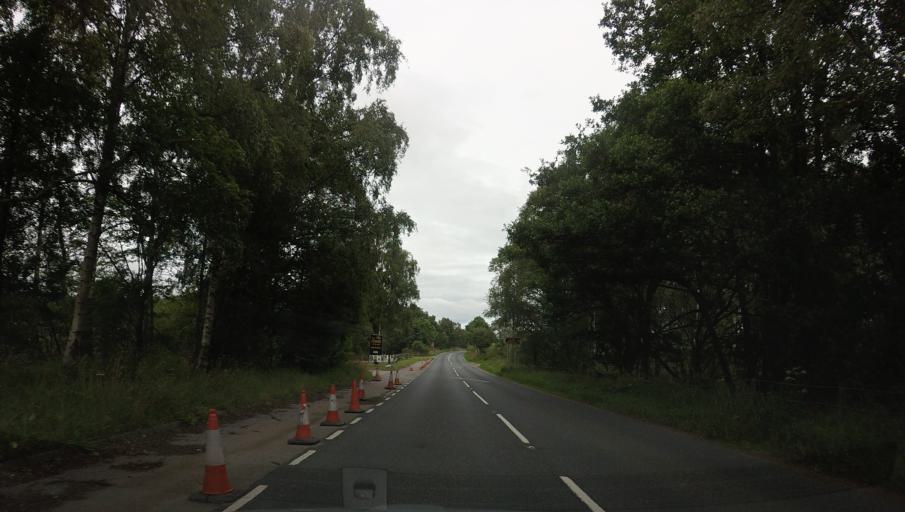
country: GB
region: Scotland
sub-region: Aberdeenshire
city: Aboyne
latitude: 57.0869
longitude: -2.7610
